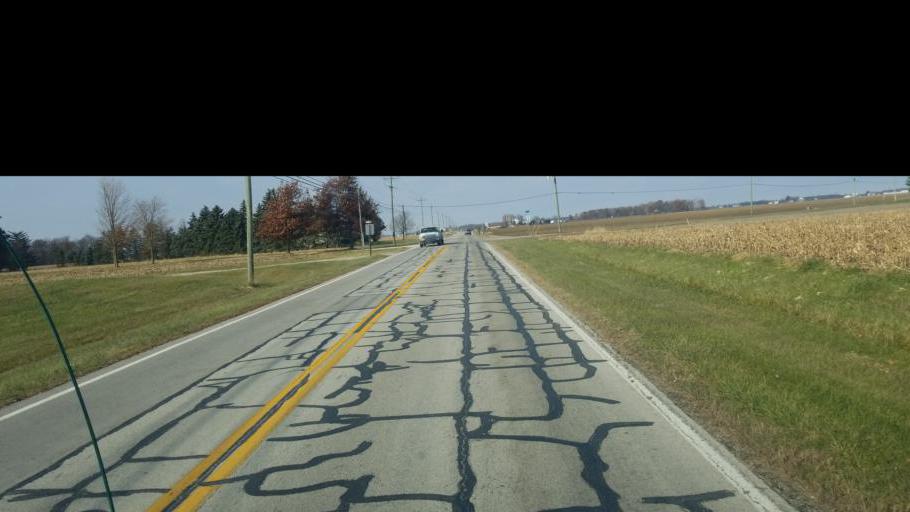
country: US
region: Ohio
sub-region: Mercer County
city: Celina
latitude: 40.5669
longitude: -84.5895
